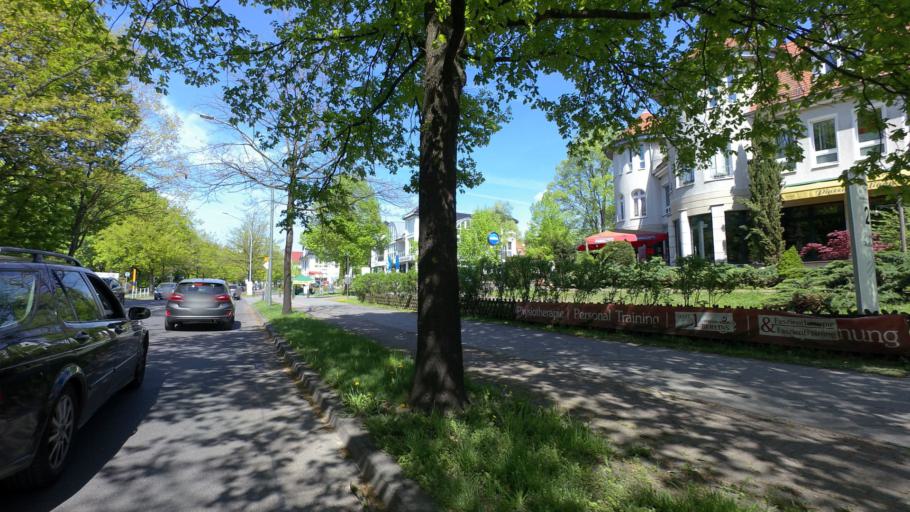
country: DE
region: Brandenburg
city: Glienicke
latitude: 52.6285
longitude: 13.3111
